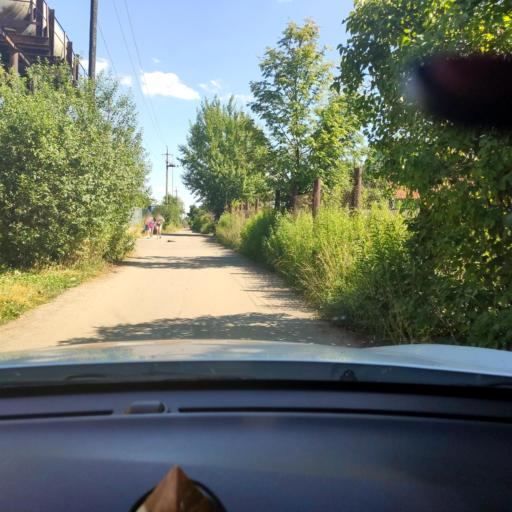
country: RU
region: Tatarstan
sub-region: Zelenodol'skiy Rayon
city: Vasil'yevo
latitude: 55.8267
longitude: 48.7443
